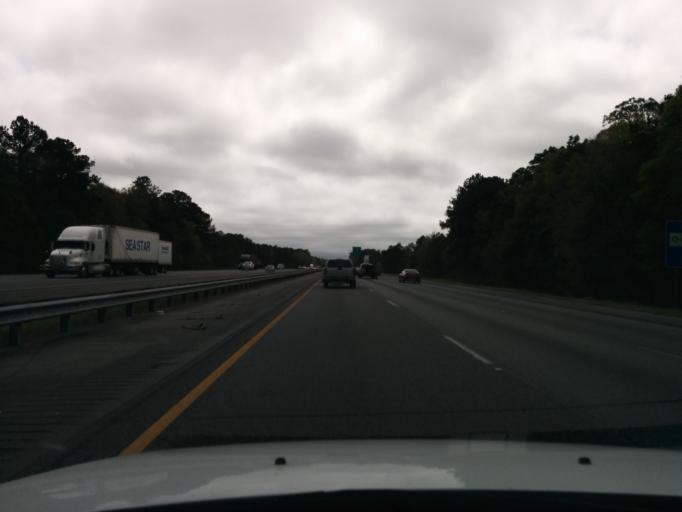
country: US
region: Georgia
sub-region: Chatham County
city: Georgetown
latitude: 32.0224
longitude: -81.2722
